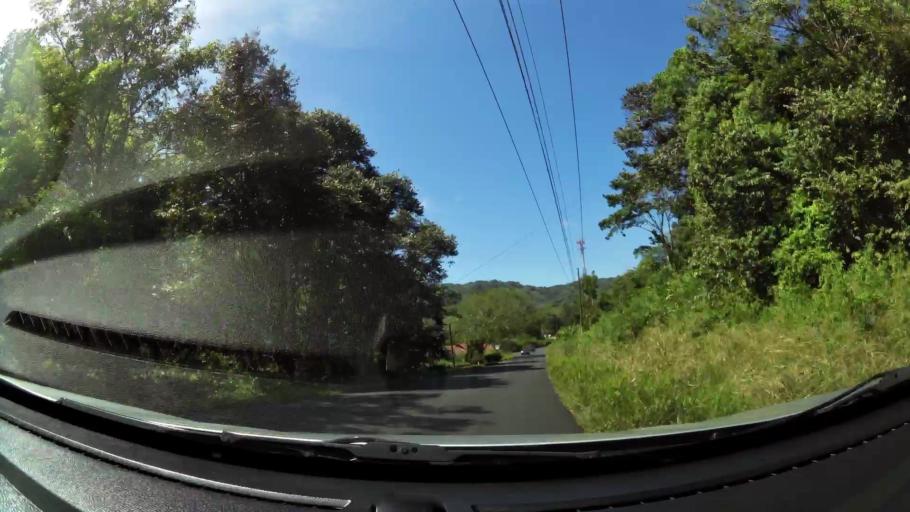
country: CR
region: San Jose
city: San Isidro
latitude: 9.2817
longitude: -83.8507
